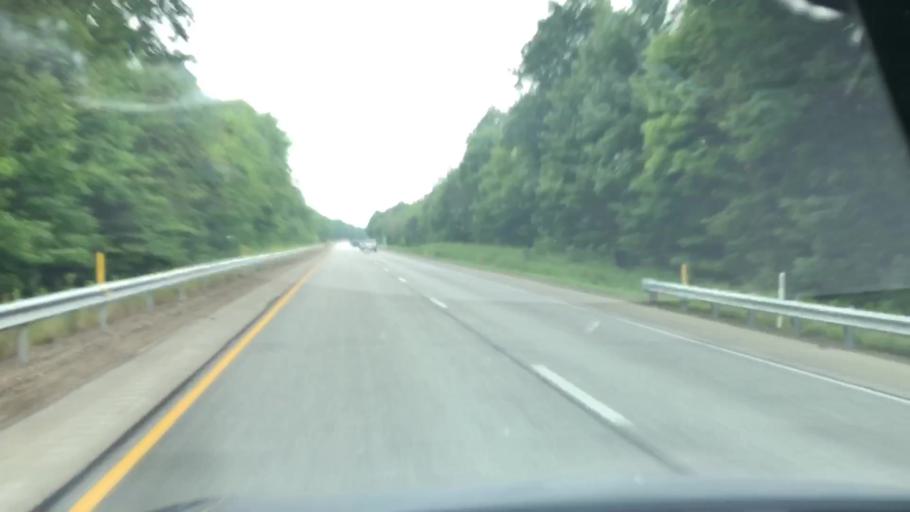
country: US
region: Pennsylvania
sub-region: Erie County
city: Edinboro
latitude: 41.9123
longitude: -80.1757
